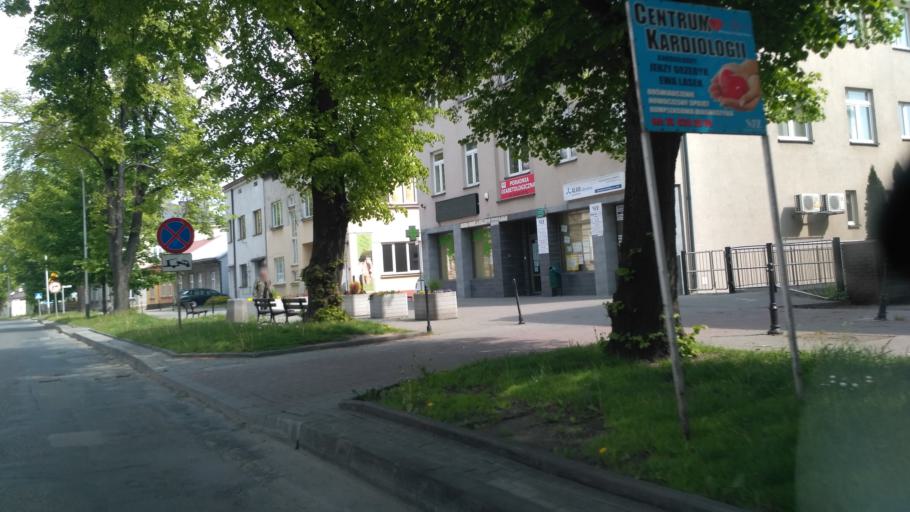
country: PL
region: Subcarpathian Voivodeship
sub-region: Powiat jaroslawski
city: Jaroslaw
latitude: 50.0194
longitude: 22.6767
